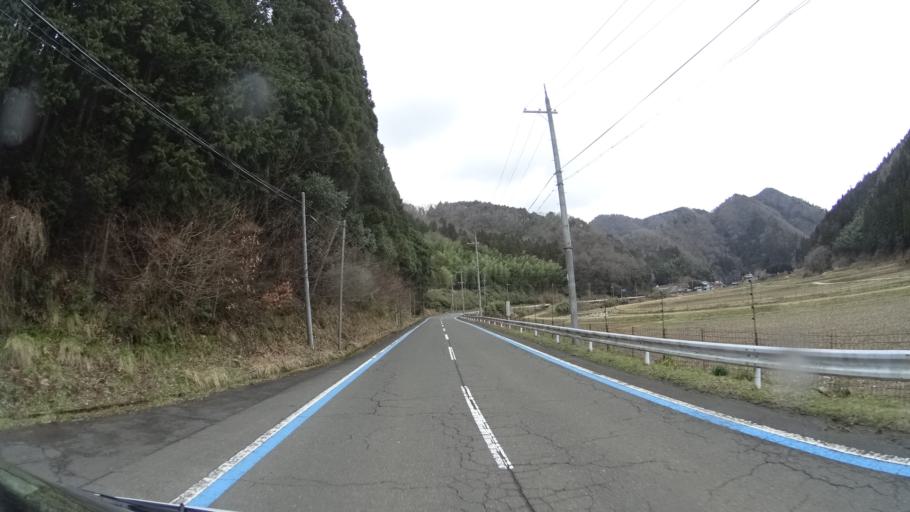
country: JP
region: Kyoto
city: Maizuru
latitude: 35.4027
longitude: 135.4154
